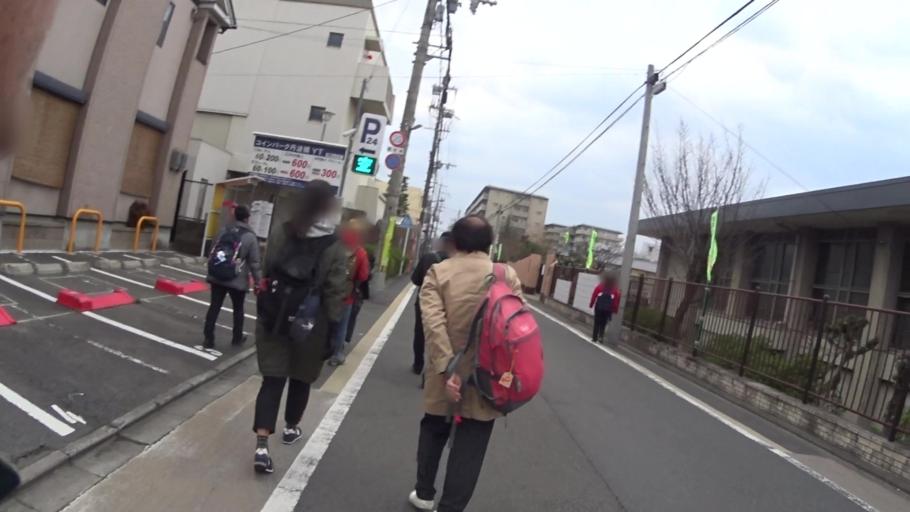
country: JP
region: Kyoto
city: Uji
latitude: 34.9388
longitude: 135.7624
